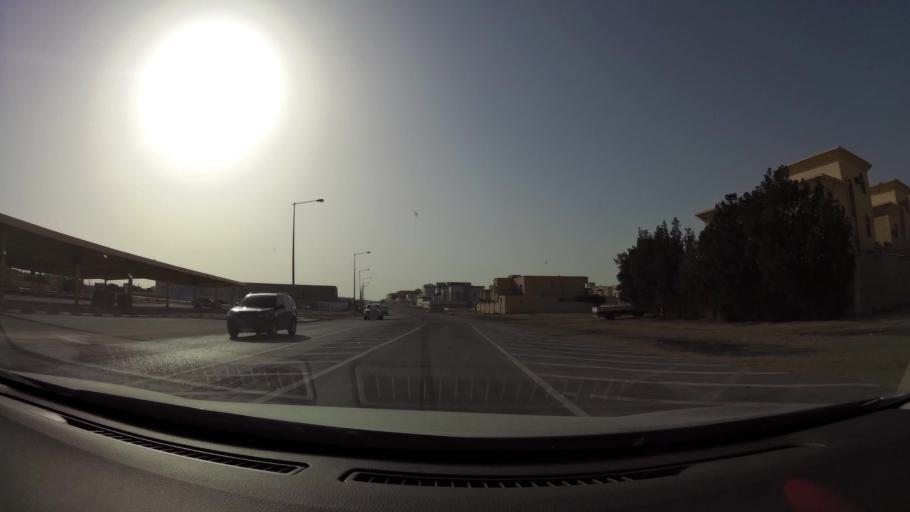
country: QA
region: Baladiyat ar Rayyan
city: Ar Rayyan
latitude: 25.3313
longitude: 51.4369
